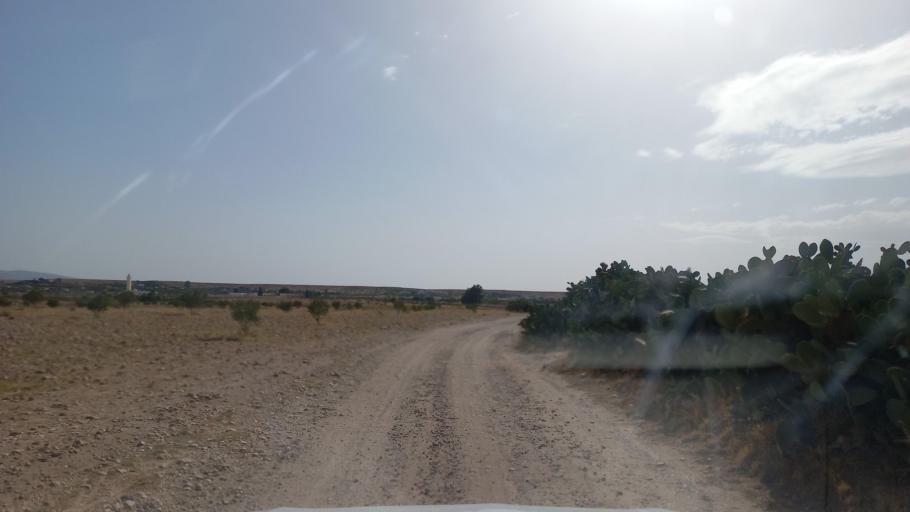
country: TN
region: Al Qasrayn
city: Kasserine
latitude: 35.2704
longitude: 8.9379
